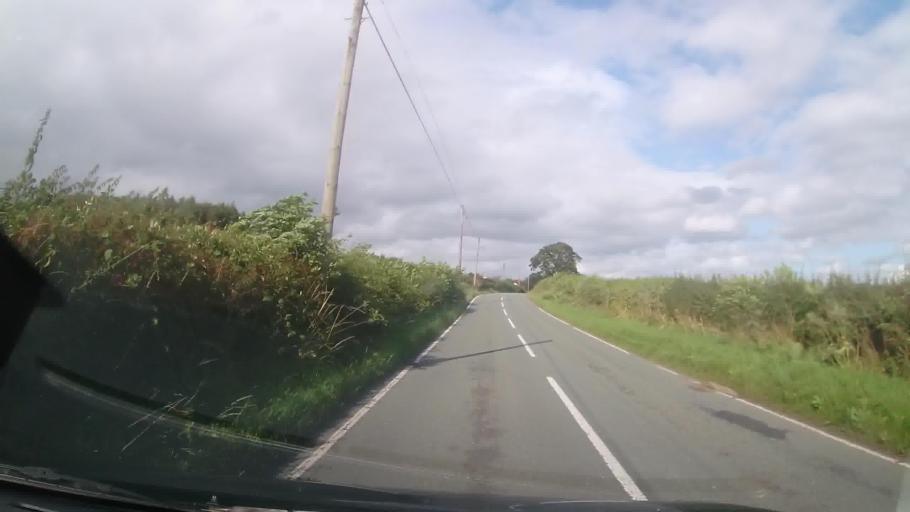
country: GB
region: England
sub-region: Shropshire
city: Lydham
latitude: 52.4995
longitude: -2.9762
